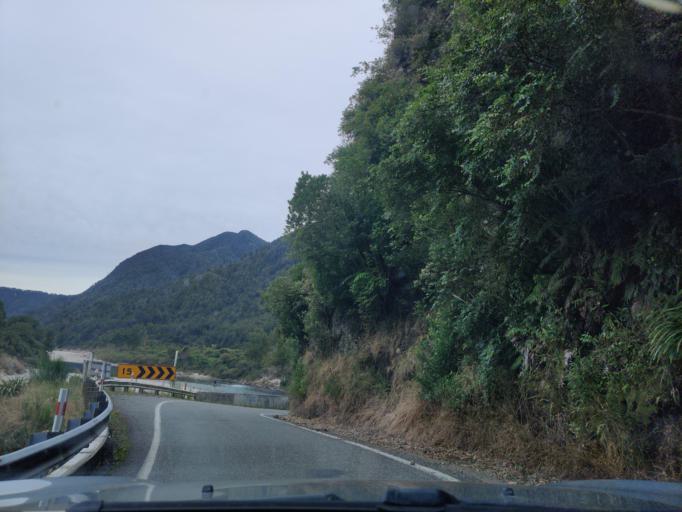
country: NZ
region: West Coast
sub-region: Buller District
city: Westport
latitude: -41.8479
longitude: 171.7426
